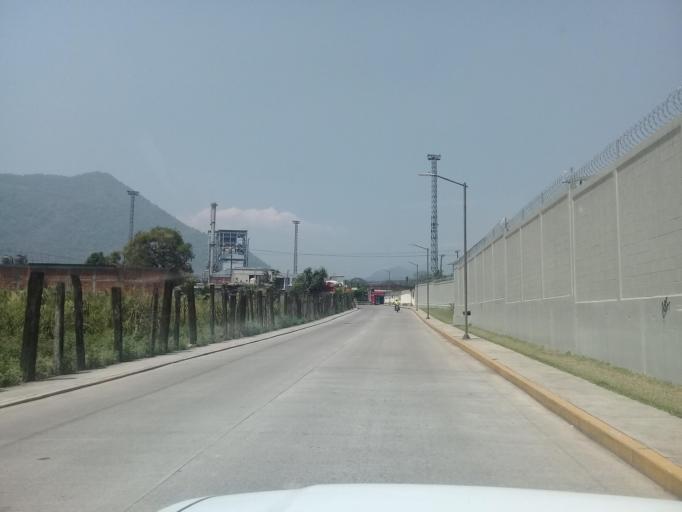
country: MX
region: Veracruz
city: Ixtac Zoquitlan
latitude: 18.8635
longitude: -97.0621
